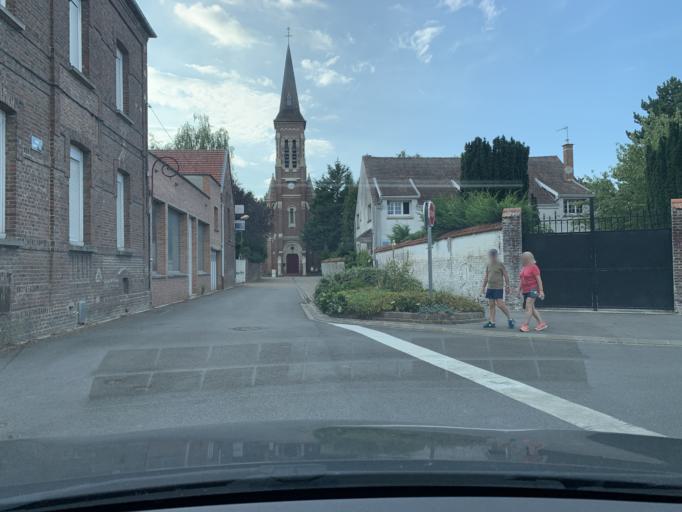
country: FR
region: Nord-Pas-de-Calais
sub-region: Departement du Nord
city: Proville
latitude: 50.1630
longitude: 3.2070
